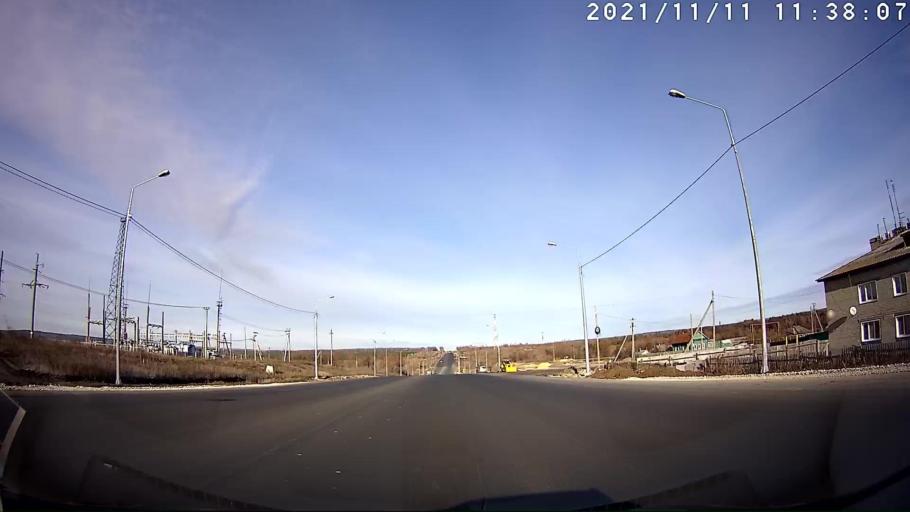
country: RU
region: Samara
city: Varlamovo
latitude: 53.3788
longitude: 48.3788
